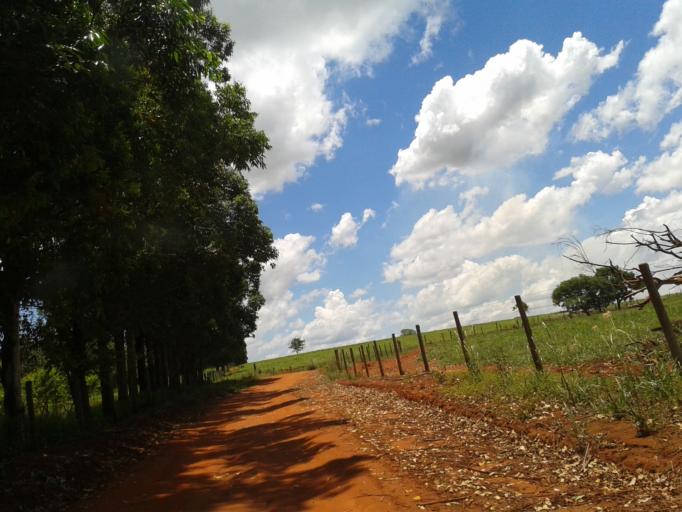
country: BR
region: Minas Gerais
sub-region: Centralina
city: Centralina
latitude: -18.7045
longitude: -49.1710
